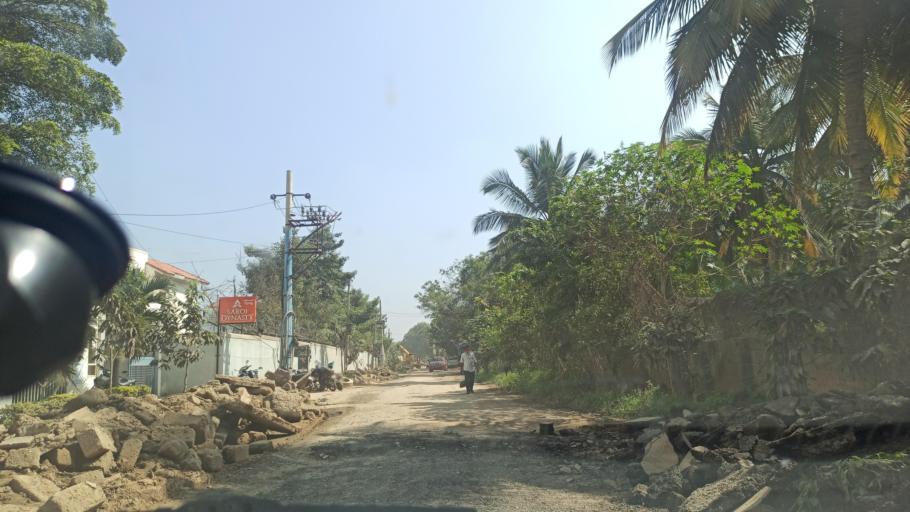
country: IN
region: Karnataka
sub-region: Bangalore Urban
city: Bangalore
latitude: 12.9155
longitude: 77.6915
